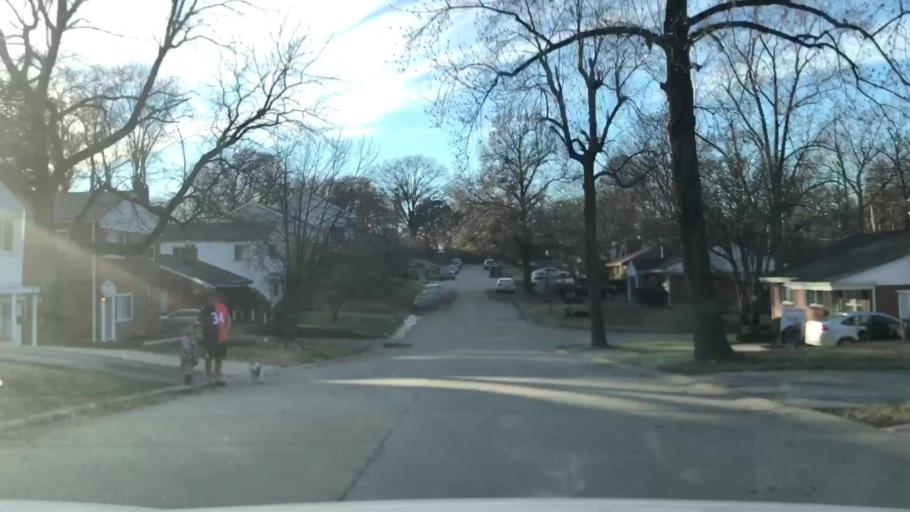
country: US
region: Missouri
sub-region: Saint Louis County
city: Brentwood
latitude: 38.6198
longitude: -90.3422
